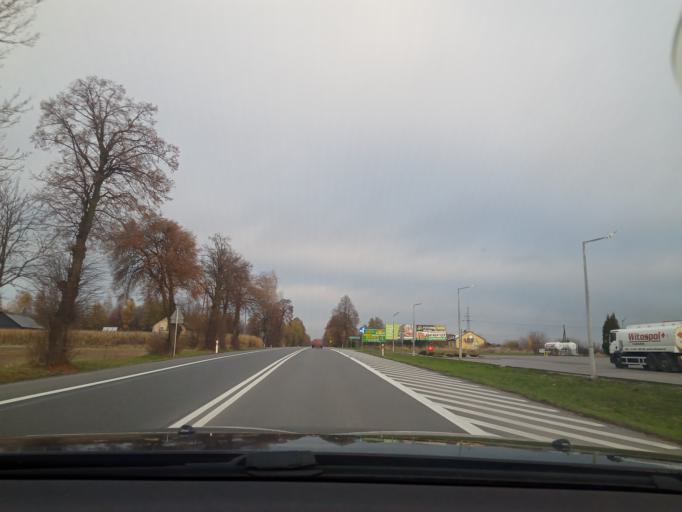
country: PL
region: Lesser Poland Voivodeship
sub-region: Powiat miechowski
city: Miechow
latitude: 50.3280
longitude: 20.0336
